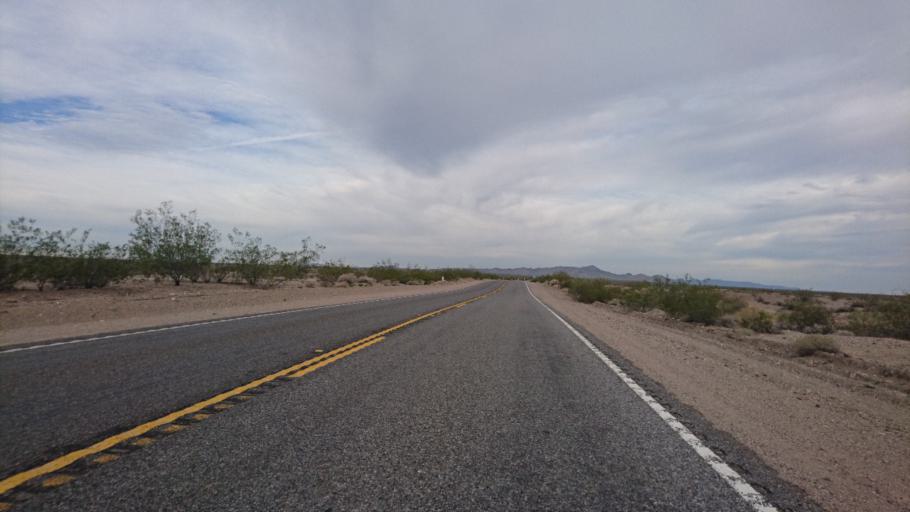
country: US
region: Arizona
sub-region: Mohave County
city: Willow Valley
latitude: 34.9366
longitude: -114.8070
